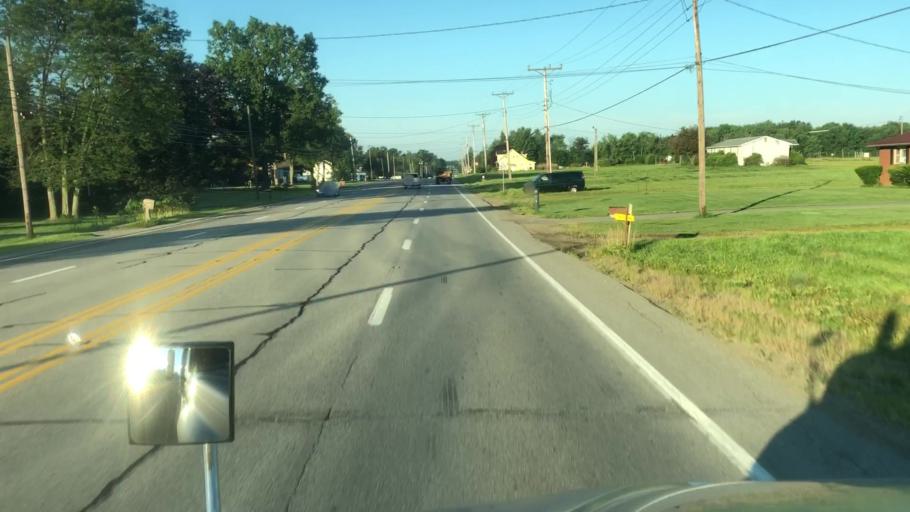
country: US
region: Pennsylvania
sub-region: Venango County
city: Franklin
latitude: 41.3674
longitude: -79.8615
